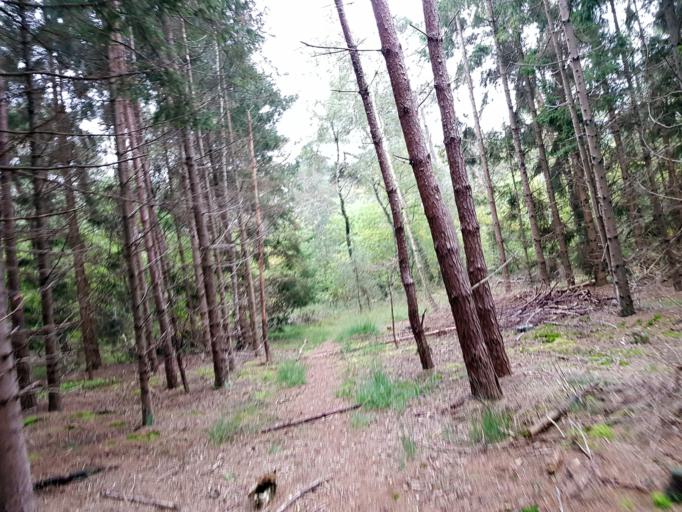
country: NL
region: Utrecht
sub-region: Gemeente Utrechtse Heuvelrug
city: Maarsbergen
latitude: 52.0503
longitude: 5.4356
